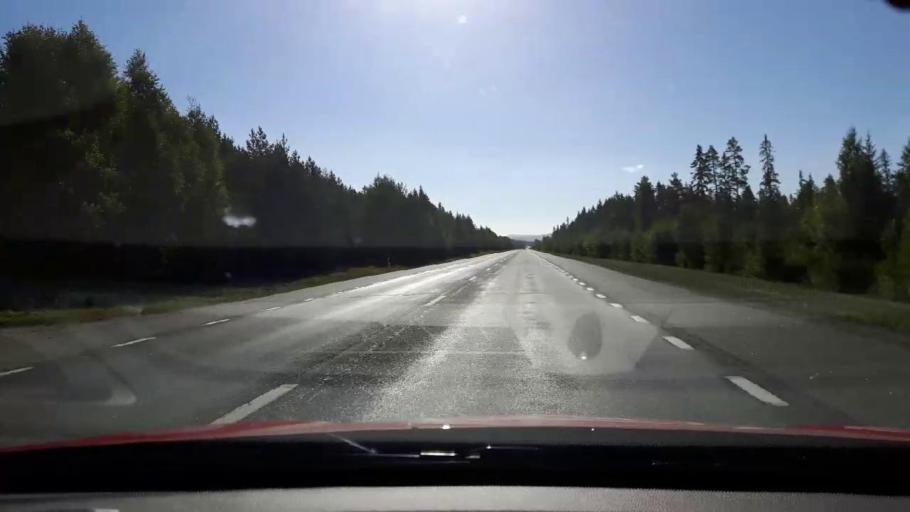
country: SE
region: Vaesternorrland
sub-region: Ange Kommun
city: Ange
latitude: 62.5910
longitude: 15.7141
